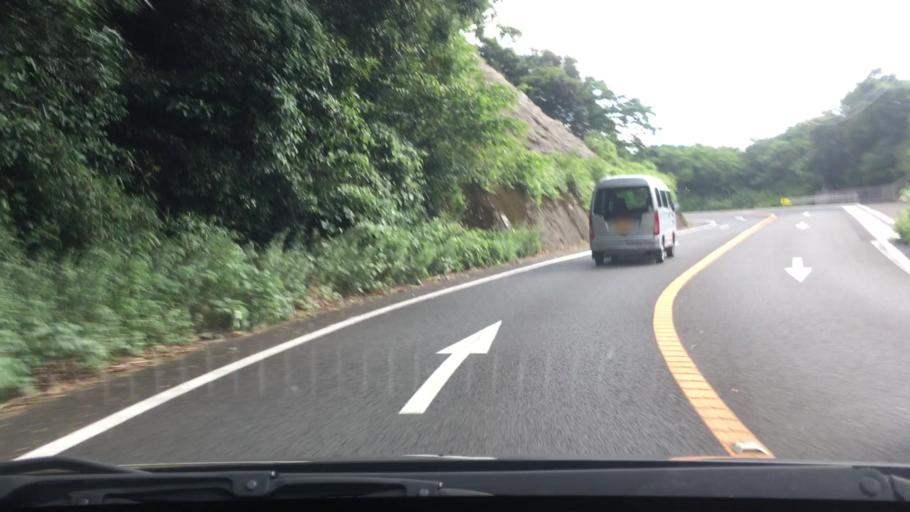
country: JP
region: Nagasaki
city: Togitsu
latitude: 32.8388
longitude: 129.7054
